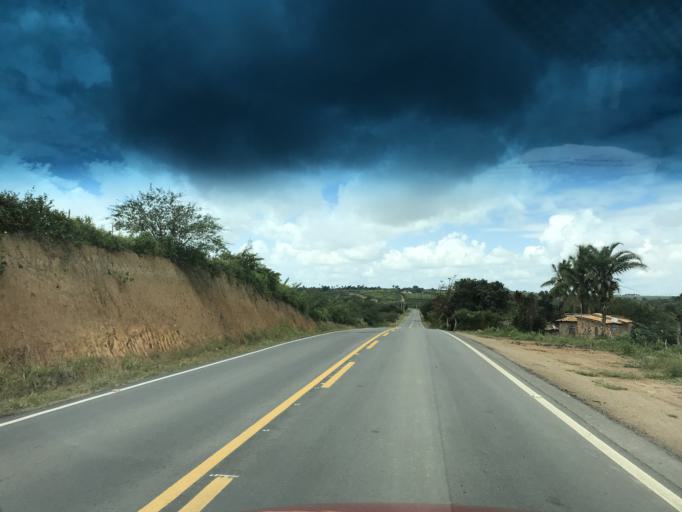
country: BR
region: Bahia
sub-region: Conceicao Do Almeida
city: Conceicao do Almeida
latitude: -12.7050
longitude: -39.2345
